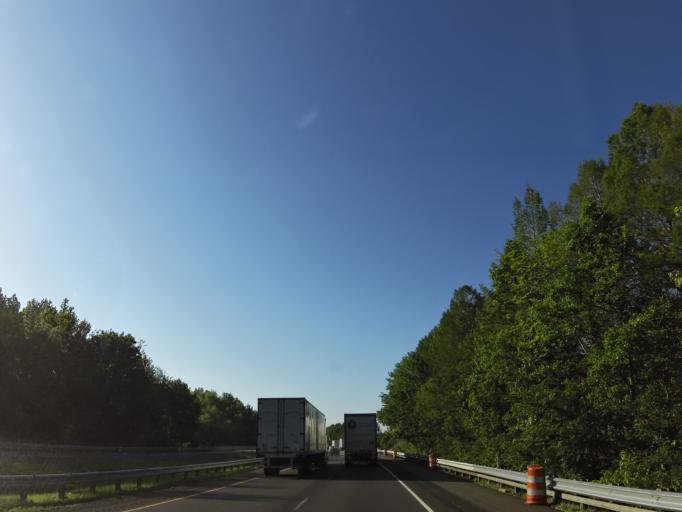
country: US
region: Indiana
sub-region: Jackson County
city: Seymour
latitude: 38.9150
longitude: -85.8337
